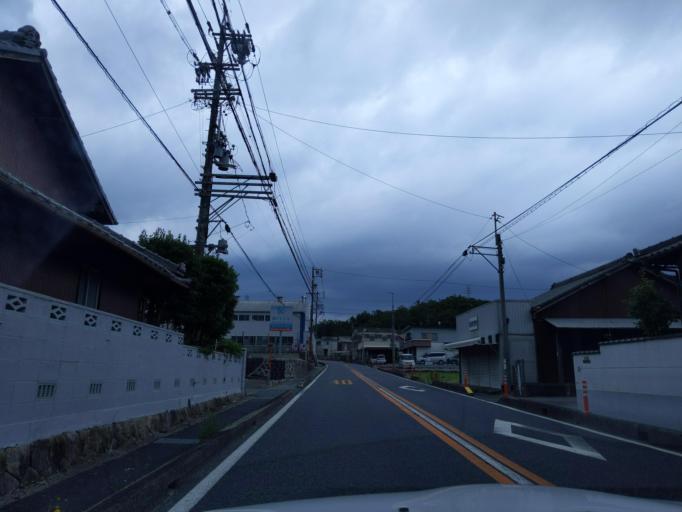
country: JP
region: Aichi
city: Seto
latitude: 35.2176
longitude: 137.1035
